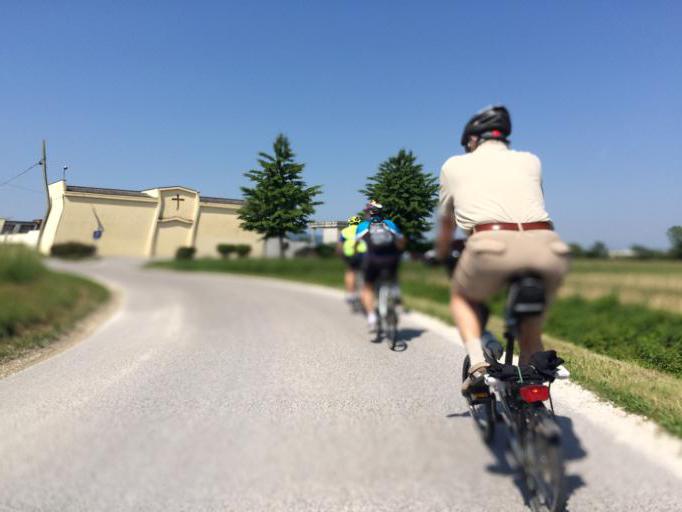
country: IT
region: Veneto
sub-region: Provincia di Vicenza
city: Grisignano di Zocco
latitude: 45.4793
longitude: 11.6828
